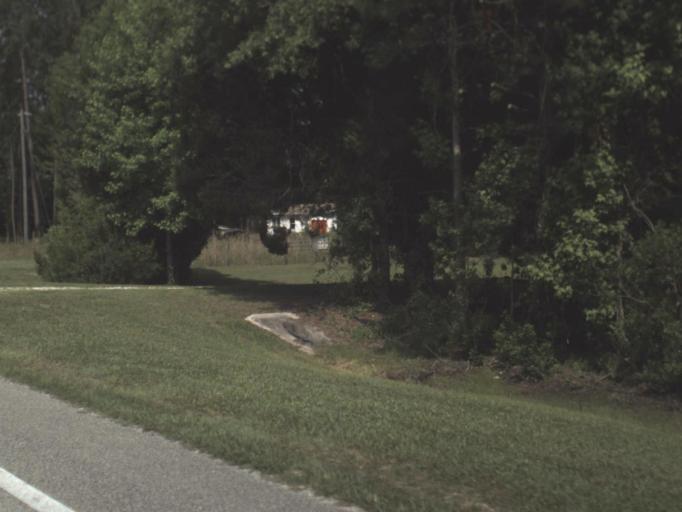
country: US
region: Florida
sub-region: Alachua County
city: Waldo
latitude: 29.7796
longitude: -82.1817
